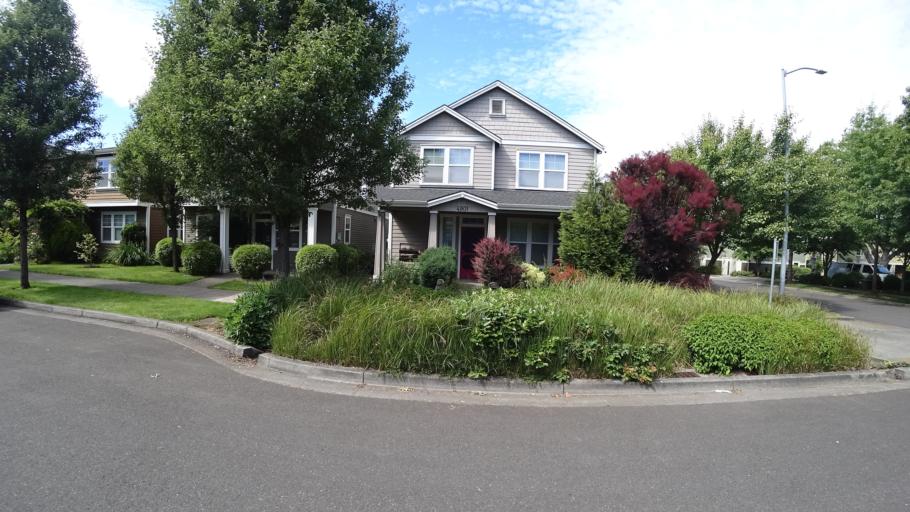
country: US
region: Washington
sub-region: Clark County
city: Vancouver
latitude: 45.5879
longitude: -122.7171
